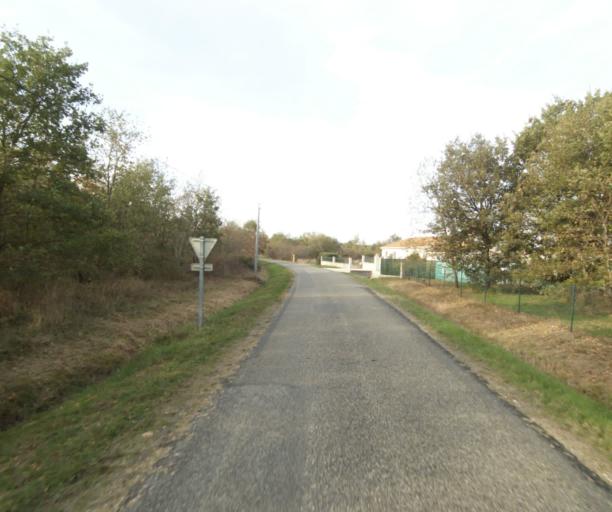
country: FR
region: Midi-Pyrenees
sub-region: Departement du Tarn-et-Garonne
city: Campsas
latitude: 43.8839
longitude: 1.3225
